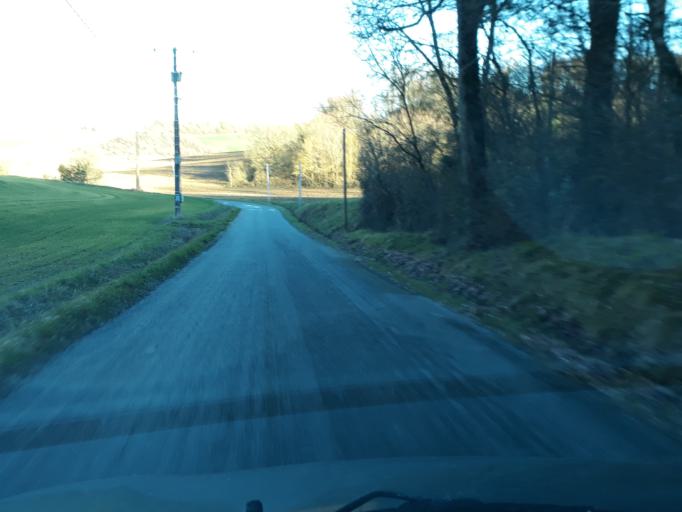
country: FR
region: Midi-Pyrenees
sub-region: Departement du Gers
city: Pavie
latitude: 43.6270
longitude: 0.6695
